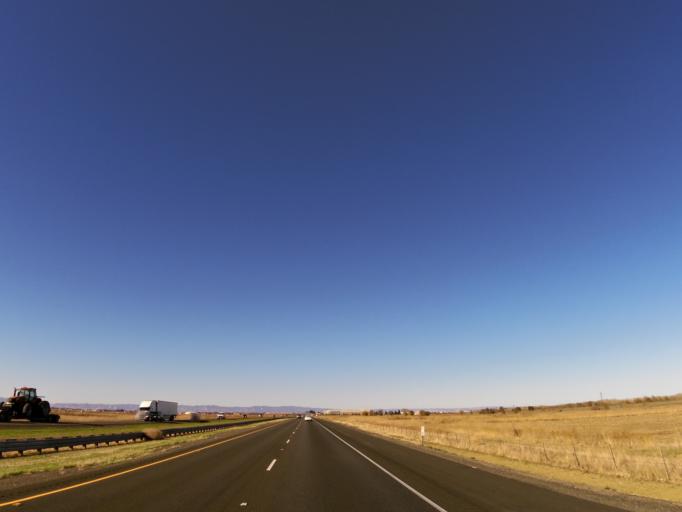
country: US
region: California
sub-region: Yolo County
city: Woodland
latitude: 38.6739
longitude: -121.6906
